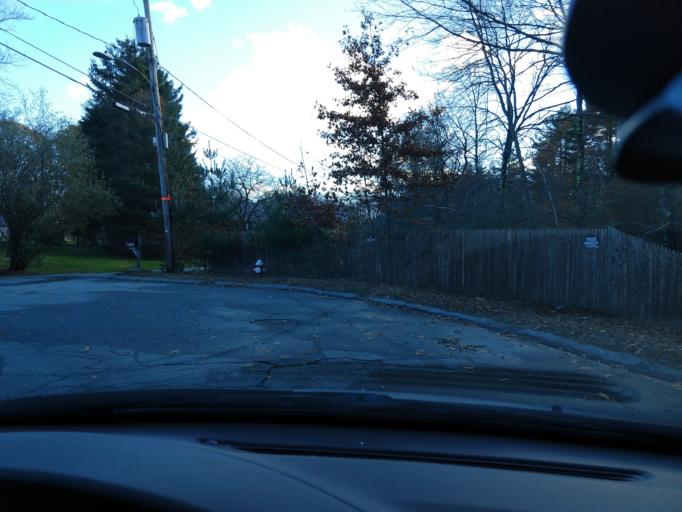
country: US
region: Massachusetts
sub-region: Middlesex County
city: Bedford
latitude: 42.5100
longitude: -71.2601
